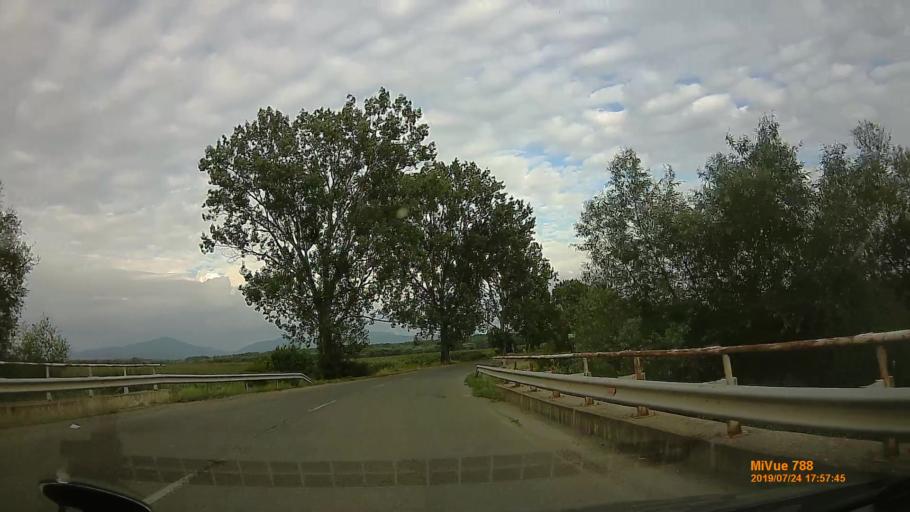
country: HU
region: Borsod-Abauj-Zemplen
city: Encs
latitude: 48.3299
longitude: 21.1381
